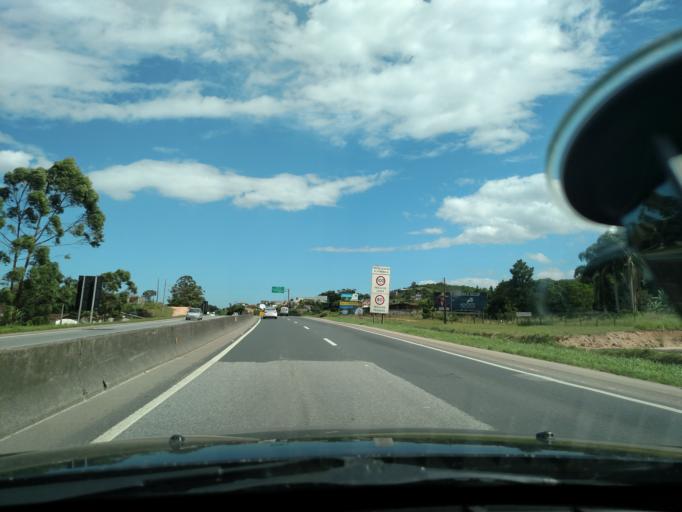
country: BR
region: Santa Catarina
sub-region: Biguacu
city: Biguacu
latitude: -27.3718
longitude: -48.6334
